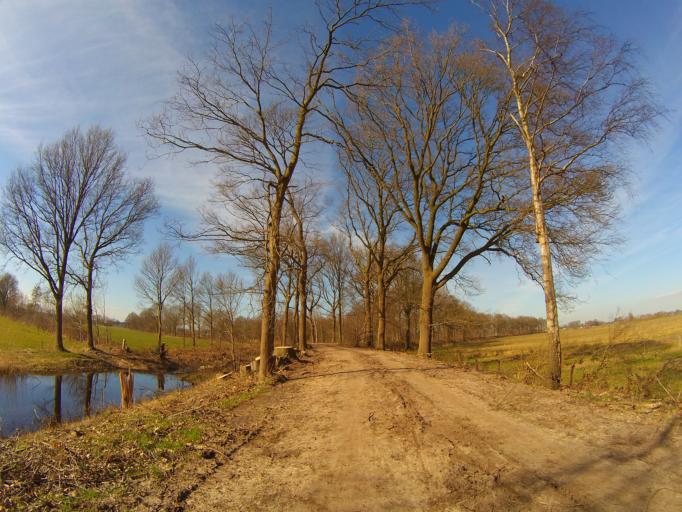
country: NL
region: Gelderland
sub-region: Gemeente Ede
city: Ederveen
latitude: 52.0797
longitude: 5.5619
